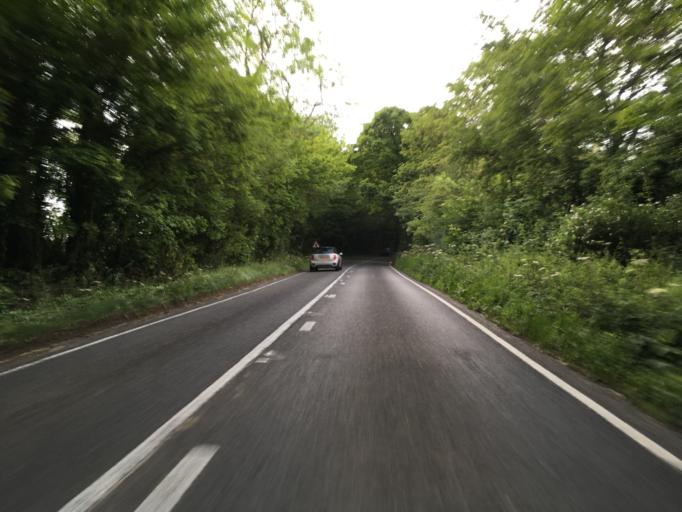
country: GB
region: England
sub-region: Oxfordshire
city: Shipton under Wychwood
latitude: 51.8912
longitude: -1.5647
